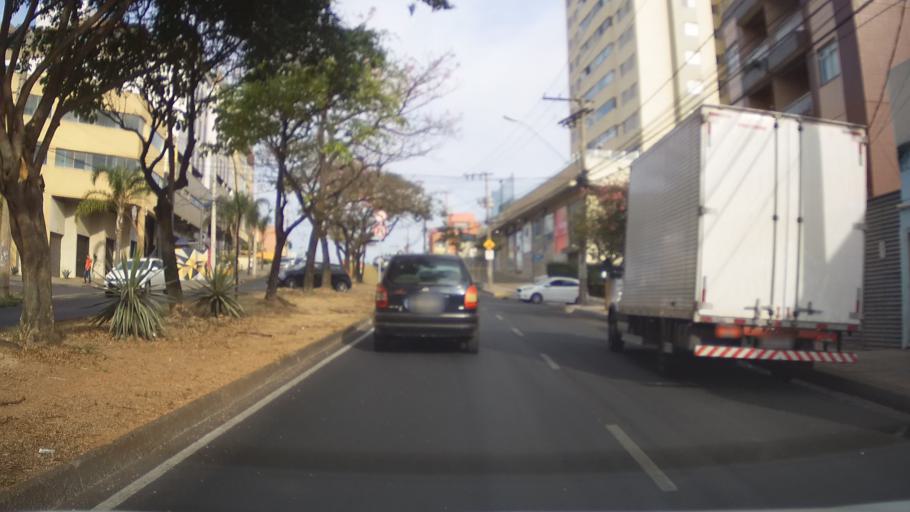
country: BR
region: Minas Gerais
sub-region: Belo Horizonte
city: Belo Horizonte
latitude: -19.8930
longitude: -43.9946
